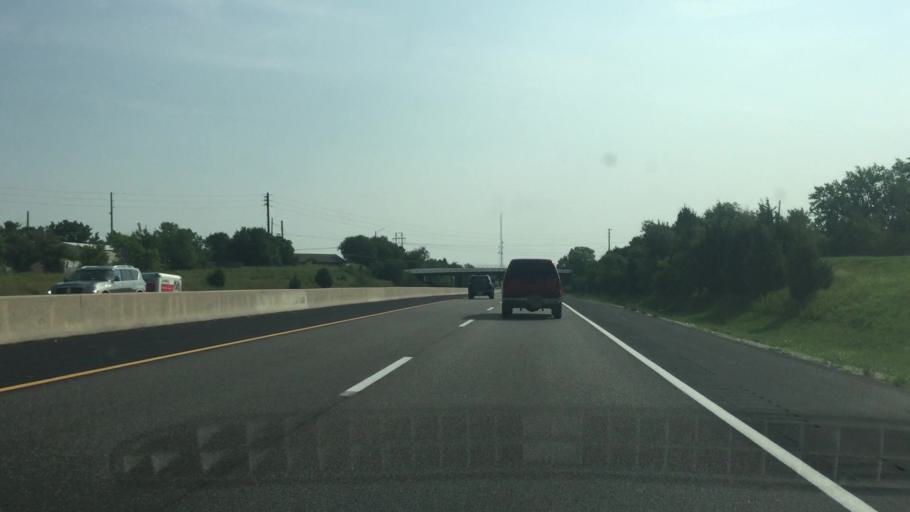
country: US
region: Kansas
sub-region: Butler County
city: Andover
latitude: 37.7072
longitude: -97.1412
